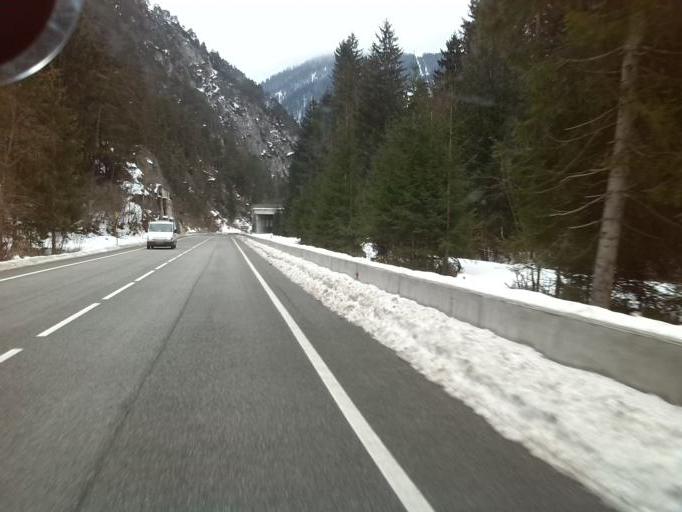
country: IT
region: Friuli Venezia Giulia
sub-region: Provincia di Udine
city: Malborghetto
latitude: 46.5069
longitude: 13.4914
